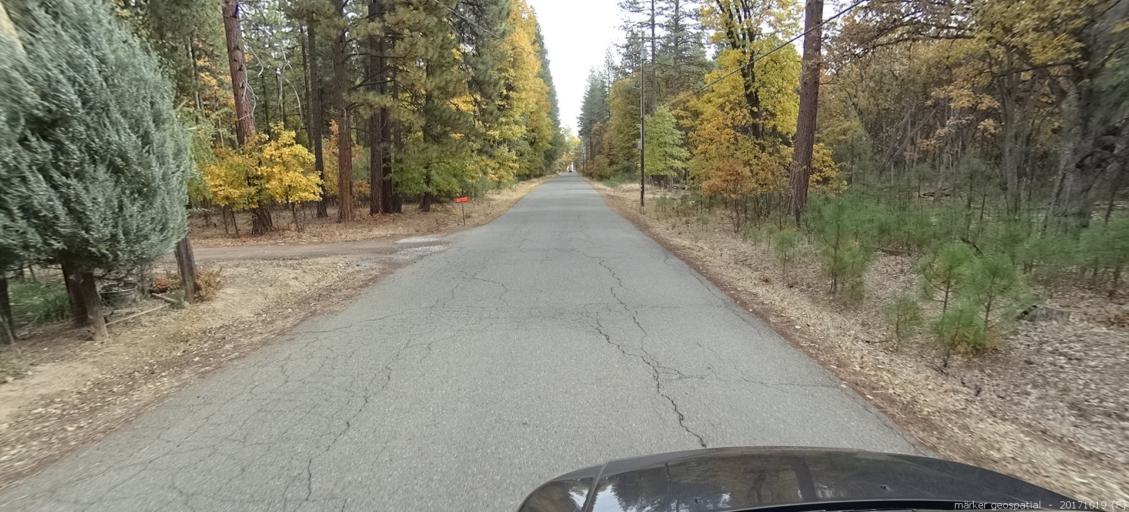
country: US
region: California
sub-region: Shasta County
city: Burney
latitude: 41.0799
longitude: -121.5231
